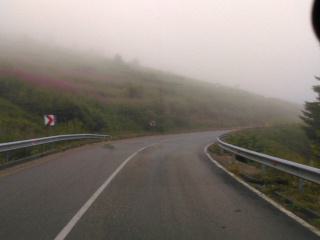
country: BG
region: Lovech
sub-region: Obshtina Troyan
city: Troyan
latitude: 42.7811
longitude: 24.6178
